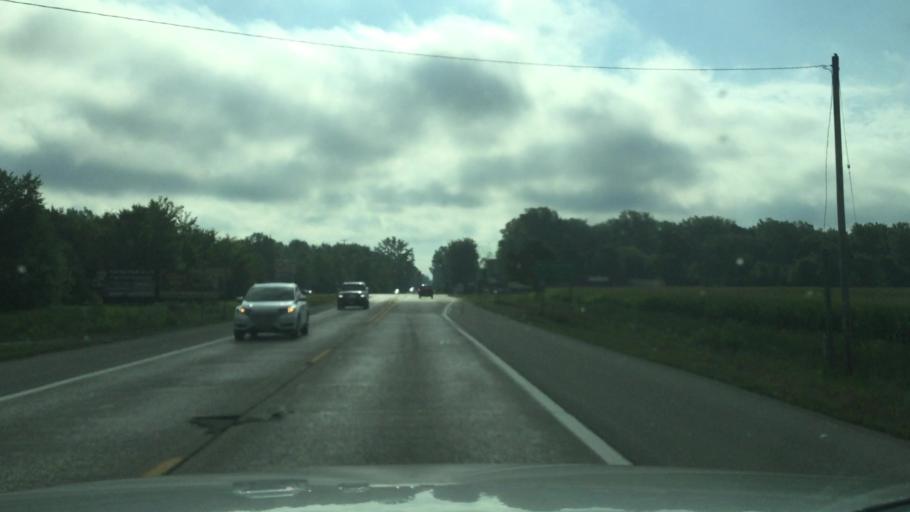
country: US
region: Michigan
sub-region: Saginaw County
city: Birch Run
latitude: 43.2500
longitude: -83.7386
